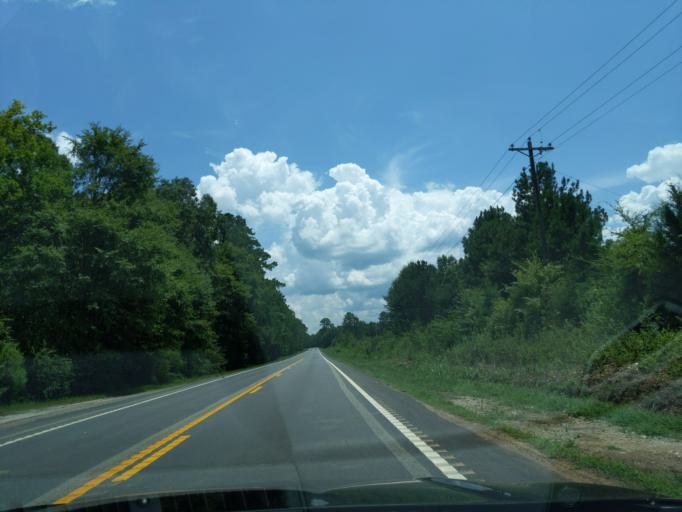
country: US
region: South Carolina
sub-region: Edgefield County
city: Edgefield
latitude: 33.8576
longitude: -81.9834
